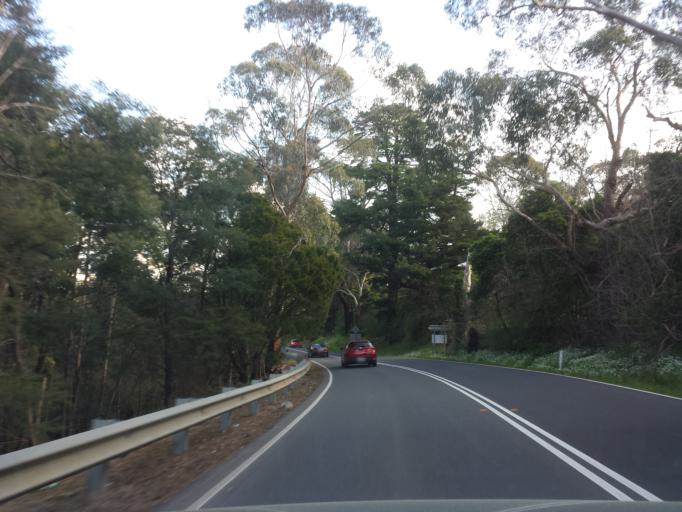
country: AU
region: Victoria
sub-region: Casey
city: Narre Warren North
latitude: -38.0011
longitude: 145.3412
